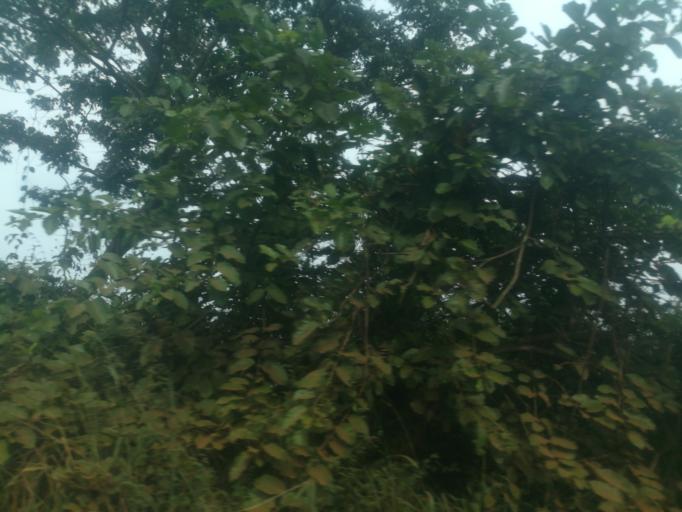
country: NG
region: Ogun
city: Ayetoro
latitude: 7.3499
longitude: 3.0539
